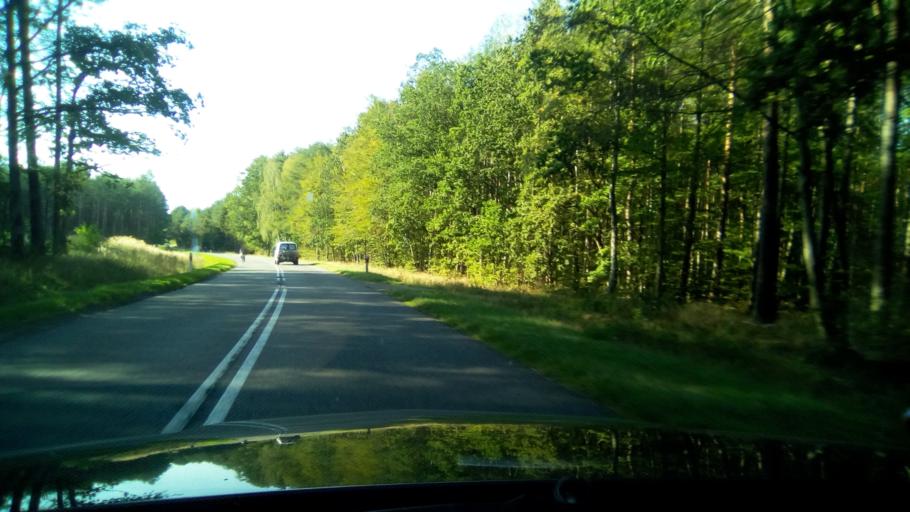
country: PL
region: West Pomeranian Voivodeship
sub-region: Powiat goleniowski
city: Przybiernow
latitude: 53.8242
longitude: 14.8053
